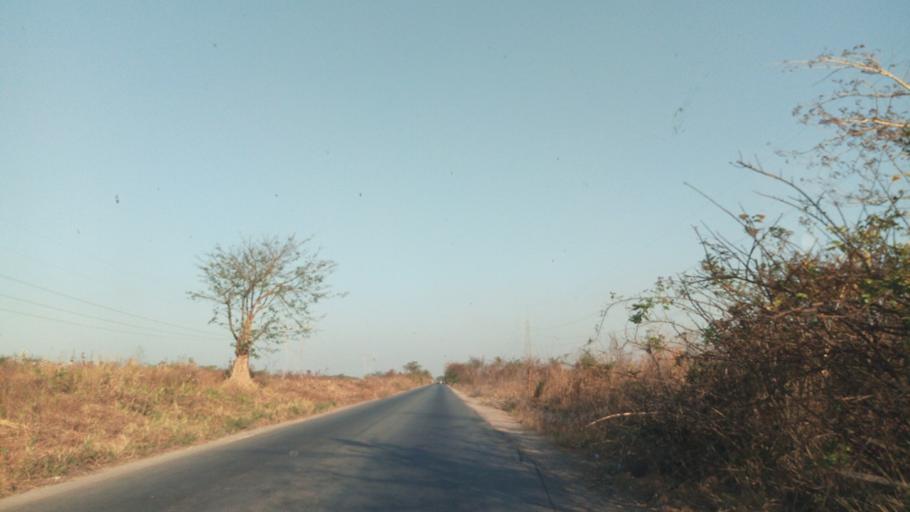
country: CD
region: Katanga
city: Likasi
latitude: -11.1084
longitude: 27.0203
